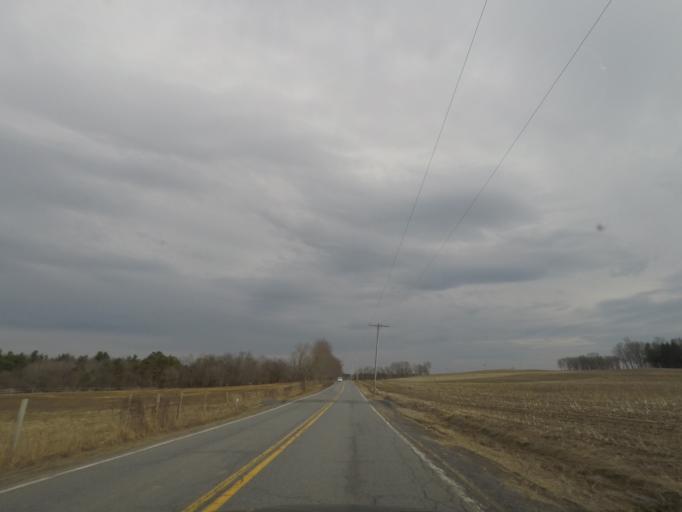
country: US
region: New York
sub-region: Washington County
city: Cambridge
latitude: 42.9622
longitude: -73.4594
